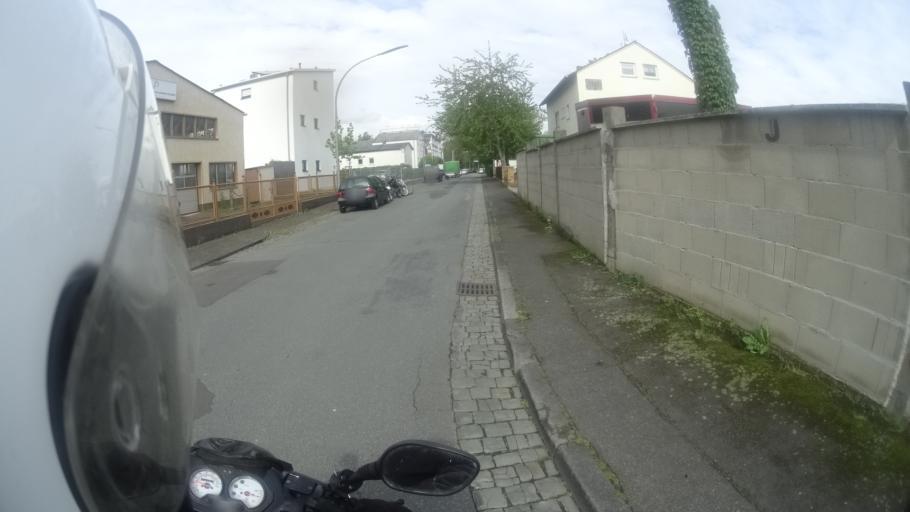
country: DE
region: Rheinland-Pfalz
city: Budenheim
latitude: 50.0488
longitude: 8.2081
